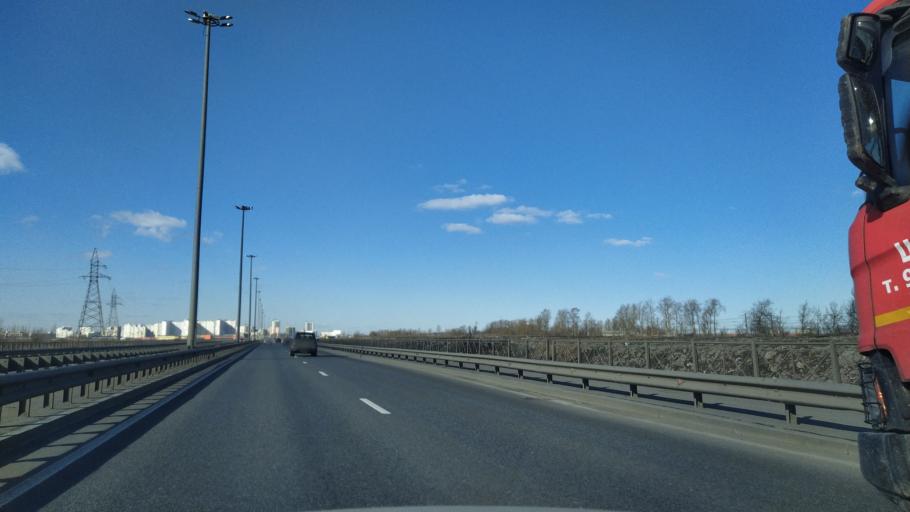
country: RU
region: St.-Petersburg
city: Shushary
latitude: 59.7798
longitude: 30.3983
